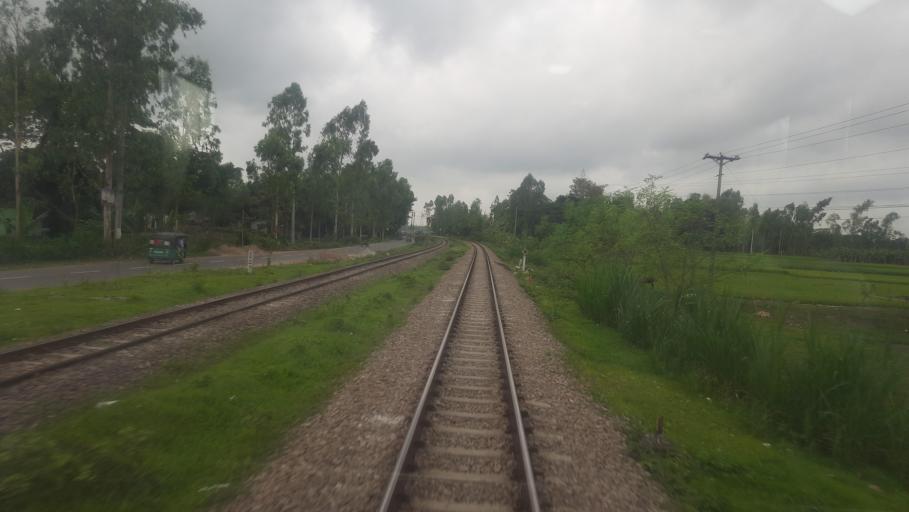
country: BD
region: Dhaka
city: Bhairab Bazar
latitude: 23.9910
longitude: 90.8621
